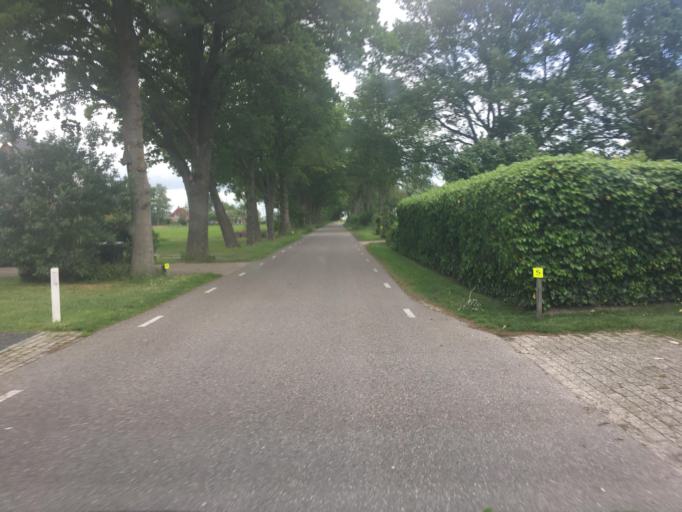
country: NL
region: Friesland
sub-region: Gemeente Heerenveen
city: Oudeschoot
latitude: 52.9180
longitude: 5.9242
